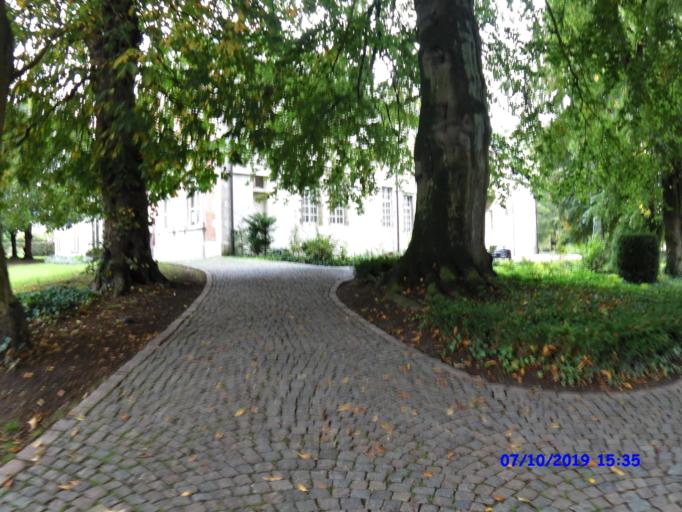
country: BE
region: Flanders
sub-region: Provincie Oost-Vlaanderen
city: Zottegem
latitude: 50.8725
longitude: 3.8095
